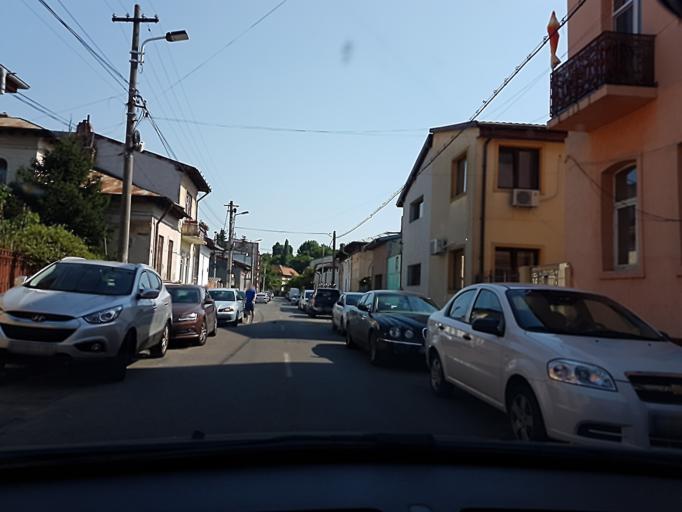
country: RO
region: Bucuresti
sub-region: Municipiul Bucuresti
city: Bucuresti
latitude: 44.4200
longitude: 26.0903
